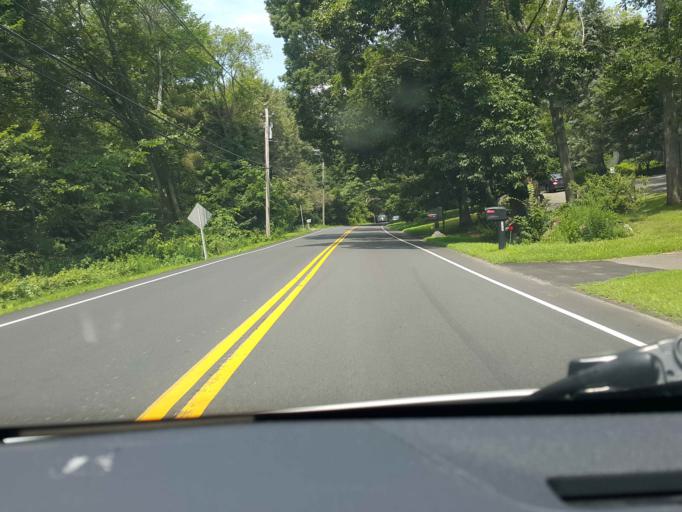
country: US
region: Connecticut
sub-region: New Haven County
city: Guilford
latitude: 41.3027
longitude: -72.6880
